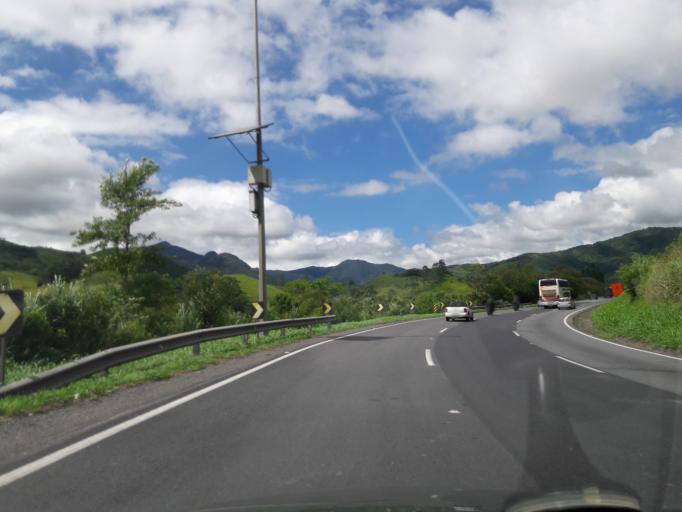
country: BR
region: Sao Paulo
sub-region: Cajati
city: Cajati
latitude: -24.8255
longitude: -48.2176
